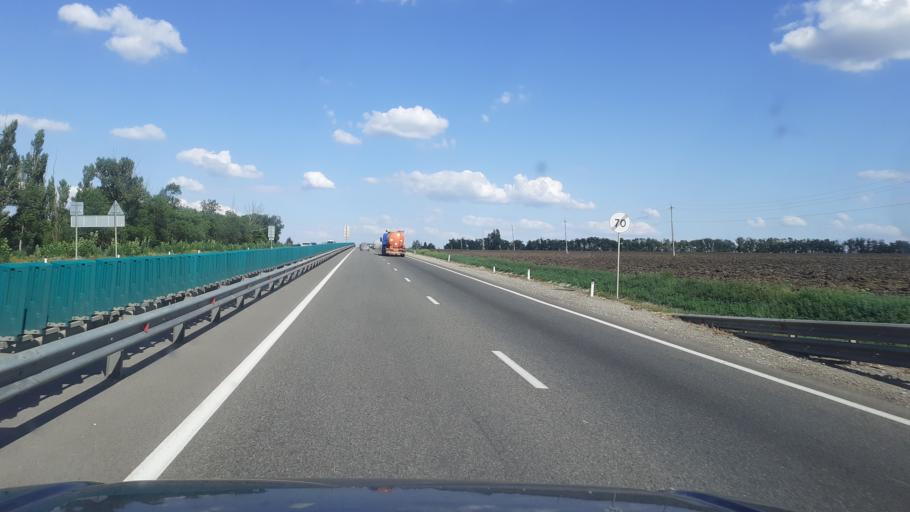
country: RU
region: Krasnodarskiy
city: Severskaya
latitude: 44.8545
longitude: 38.7123
